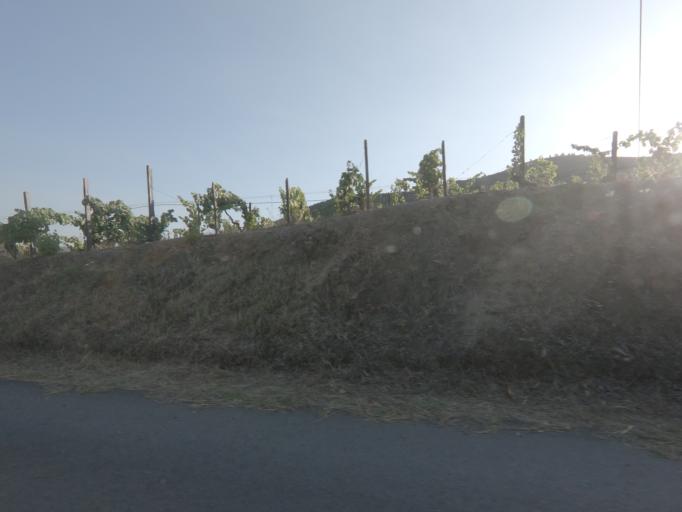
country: PT
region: Vila Real
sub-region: Sabrosa
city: Vilela
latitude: 41.1940
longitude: -7.6401
